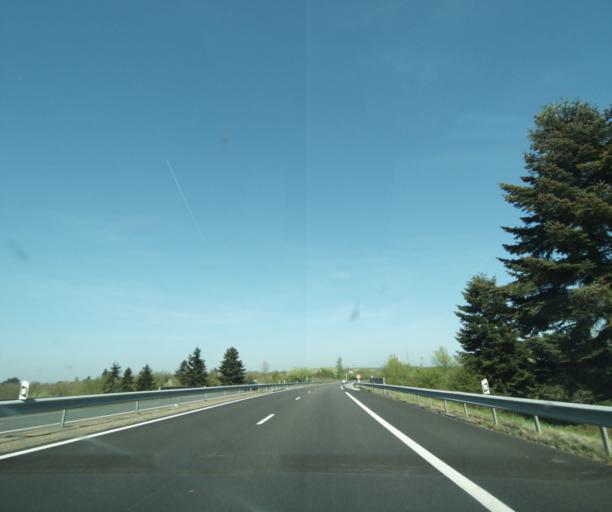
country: FR
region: Bourgogne
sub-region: Departement de la Nievre
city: La Charite-sur-Loire
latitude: 47.1349
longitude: 3.0435
